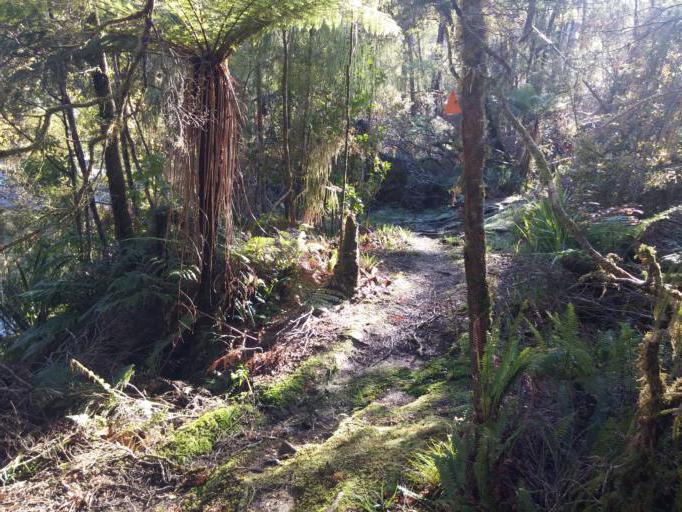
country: NZ
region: West Coast
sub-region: Grey District
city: Greymouth
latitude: -42.1200
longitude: 171.3725
